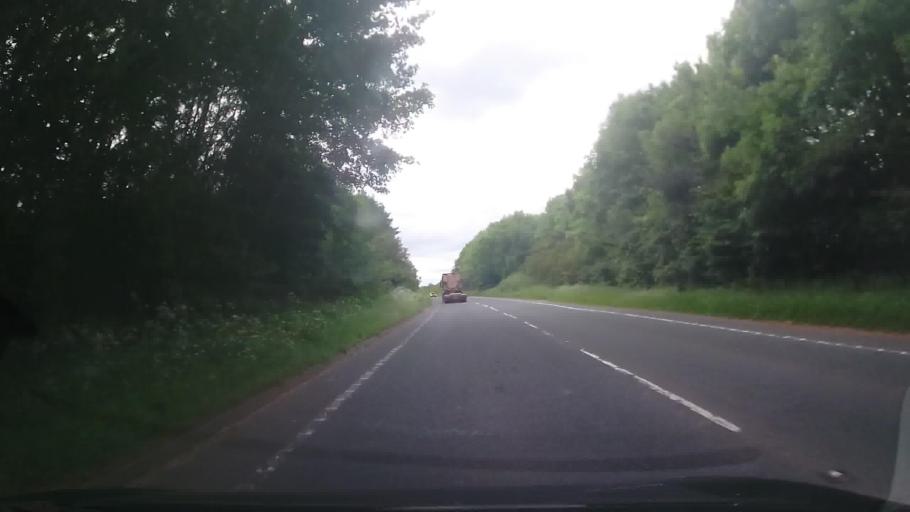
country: GB
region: England
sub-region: Telford and Wrekin
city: Newport
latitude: 52.7761
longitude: -2.3671
